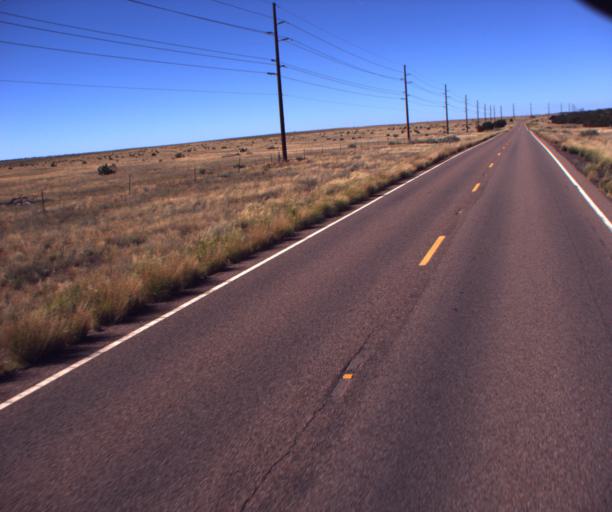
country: US
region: Arizona
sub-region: Navajo County
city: Taylor
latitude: 34.4825
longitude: -110.2944
